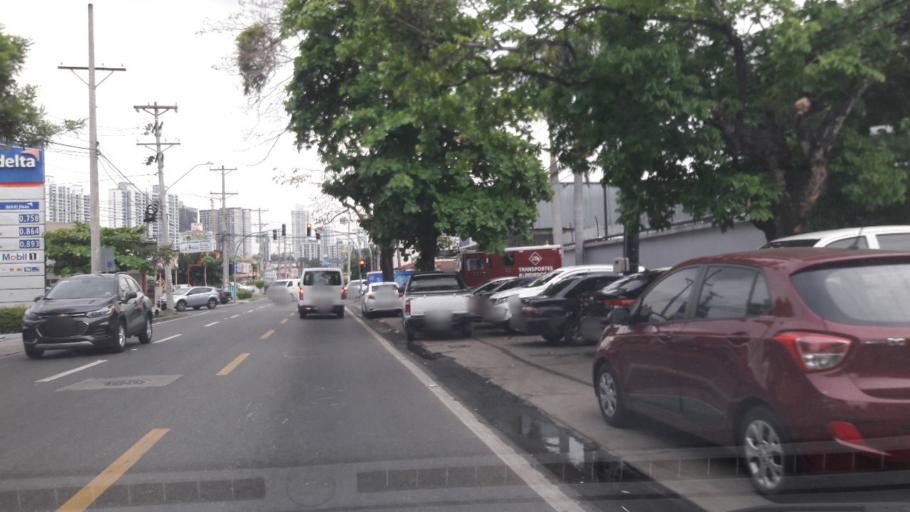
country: PA
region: Panama
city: Panama
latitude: 9.0067
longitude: -79.5011
